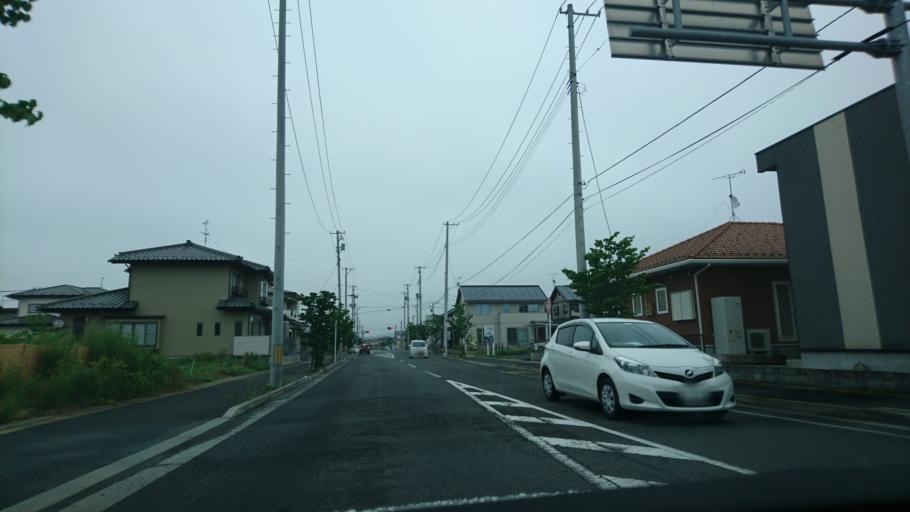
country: JP
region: Iwate
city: Ichinoseki
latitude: 38.9269
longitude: 141.1432
